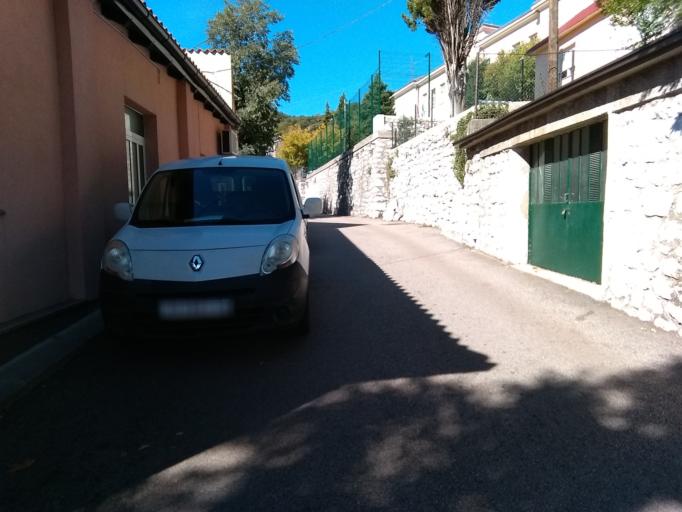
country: HR
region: Primorsko-Goranska
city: Bakar
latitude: 45.3078
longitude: 14.5355
